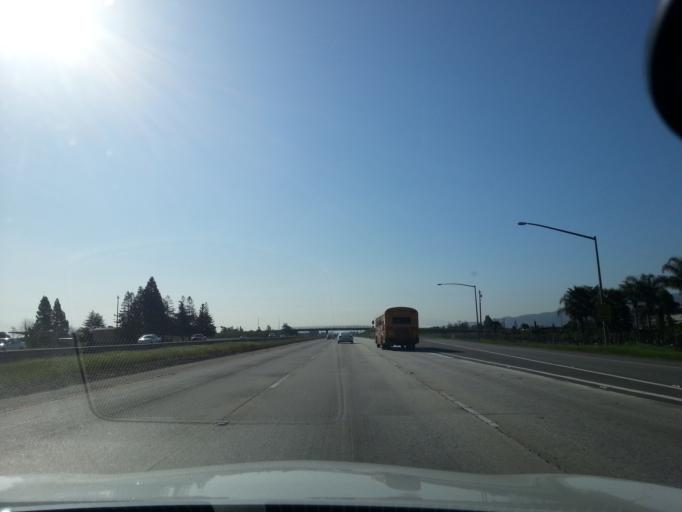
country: US
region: California
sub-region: Santa Clara County
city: San Martin
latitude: 37.0638
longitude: -121.5866
